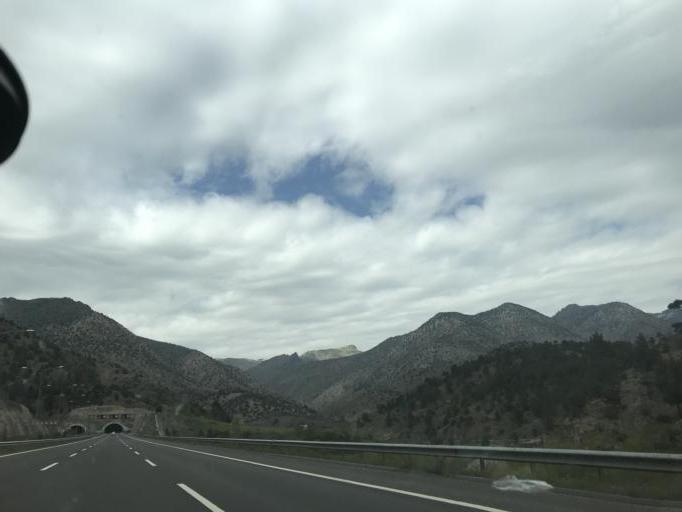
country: TR
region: Nigde
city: Ciftehan
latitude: 37.5168
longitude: 34.8177
